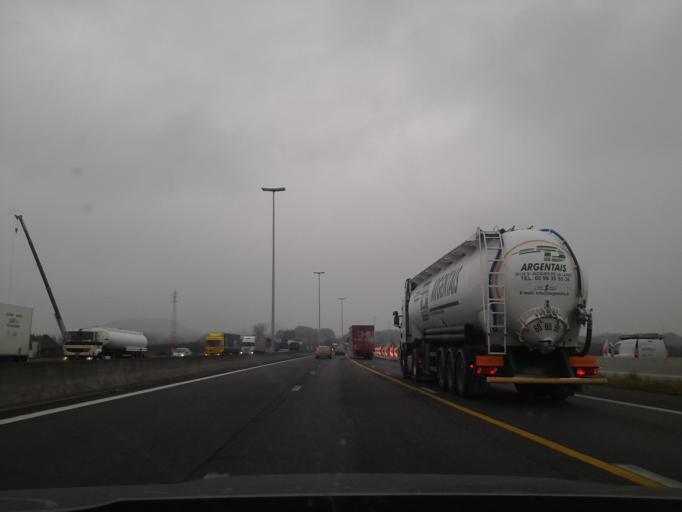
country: BE
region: Wallonia
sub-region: Province du Hainaut
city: Mons
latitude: 50.4597
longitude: 3.9243
